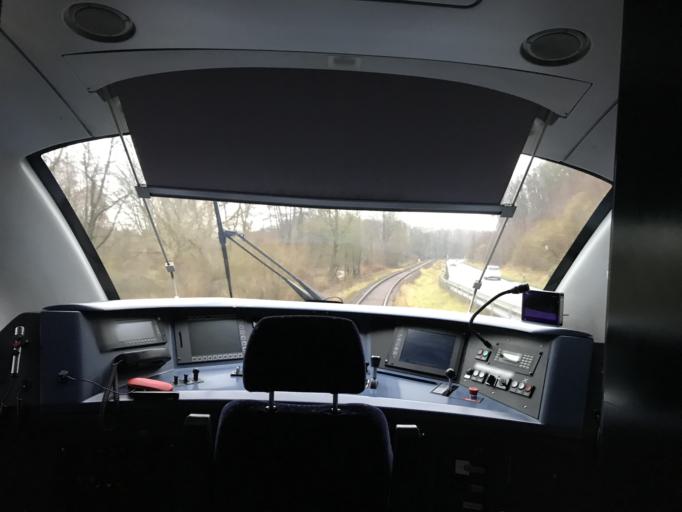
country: DE
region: Hesse
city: Fritzlar
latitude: 51.1246
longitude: 9.2386
